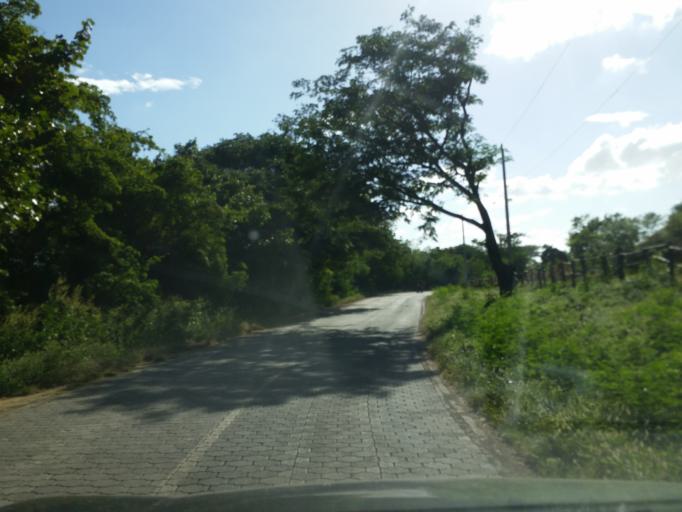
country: NI
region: Rivas
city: San Juan del Sur
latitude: 11.2616
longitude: -85.8727
